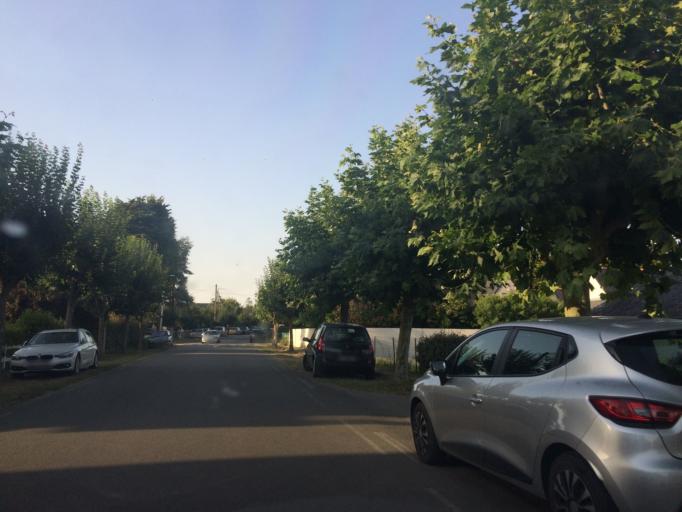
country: FR
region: Brittany
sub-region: Departement du Morbihan
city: Damgan
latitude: 47.5140
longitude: -2.5543
